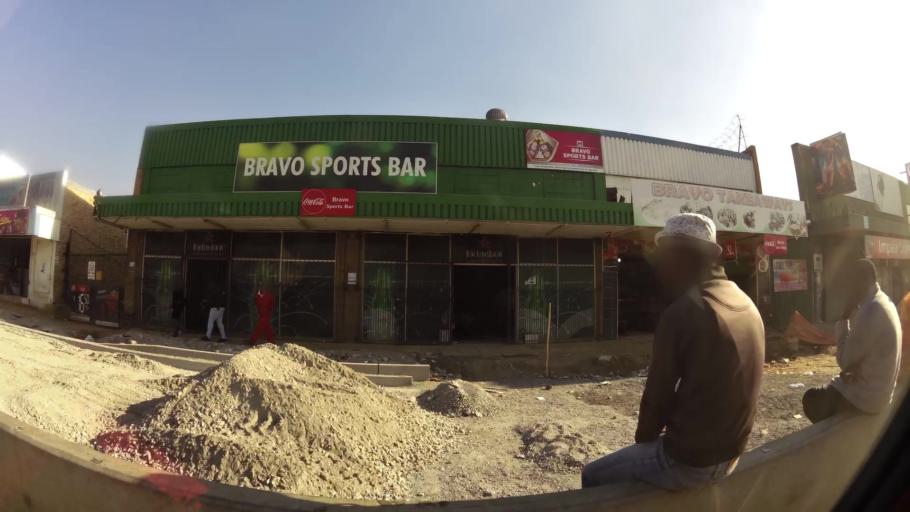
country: ZA
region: North-West
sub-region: Bojanala Platinum District Municipality
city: Rustenburg
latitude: -25.6651
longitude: 27.2358
